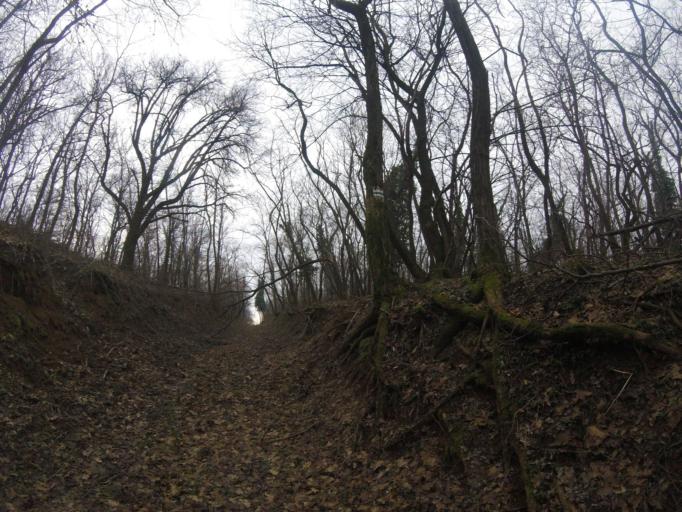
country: HU
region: Baranya
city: Pecsvarad
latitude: 46.1370
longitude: 18.5218
